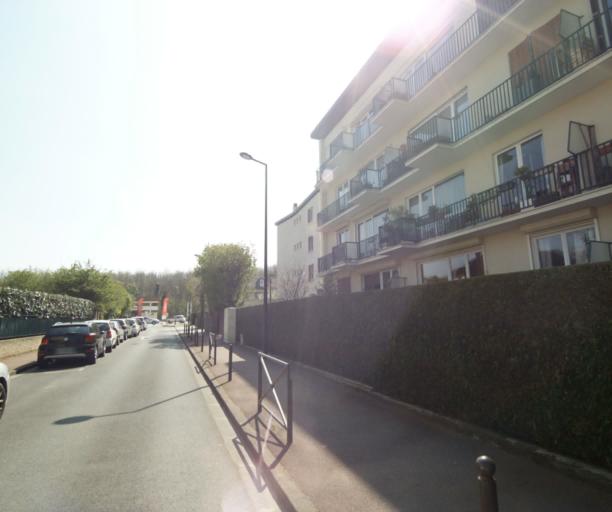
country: FR
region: Ile-de-France
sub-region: Departement des Hauts-de-Seine
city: Sevres
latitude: 48.8138
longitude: 2.2163
